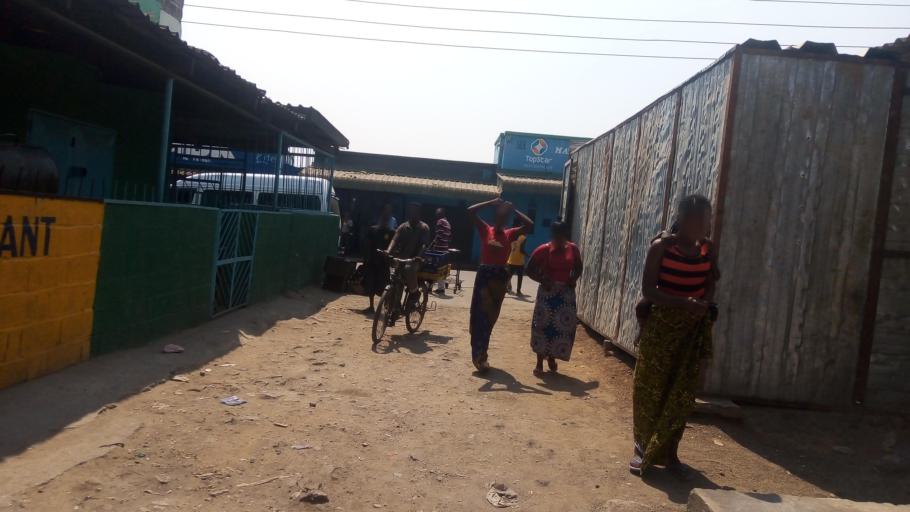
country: ZM
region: Lusaka
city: Lusaka
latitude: -15.4464
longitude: 28.3790
